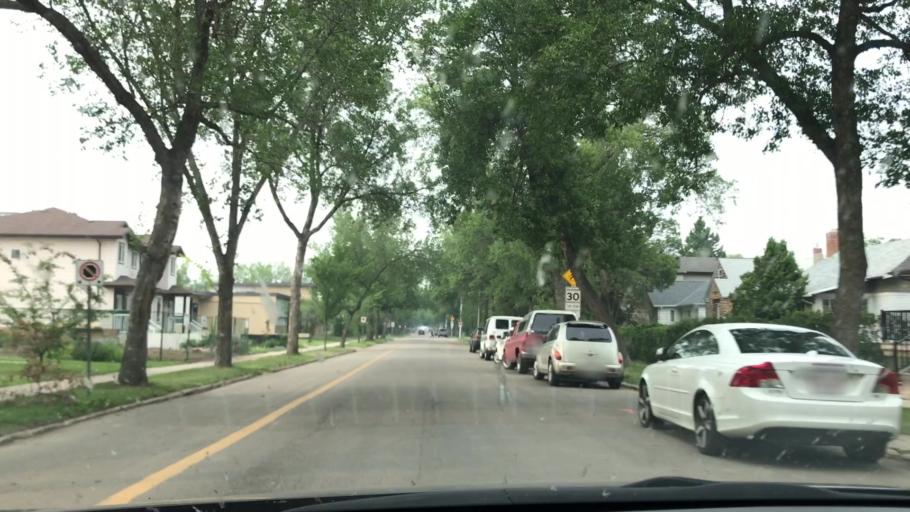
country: CA
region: Alberta
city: Edmonton
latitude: 53.5623
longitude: -113.5412
